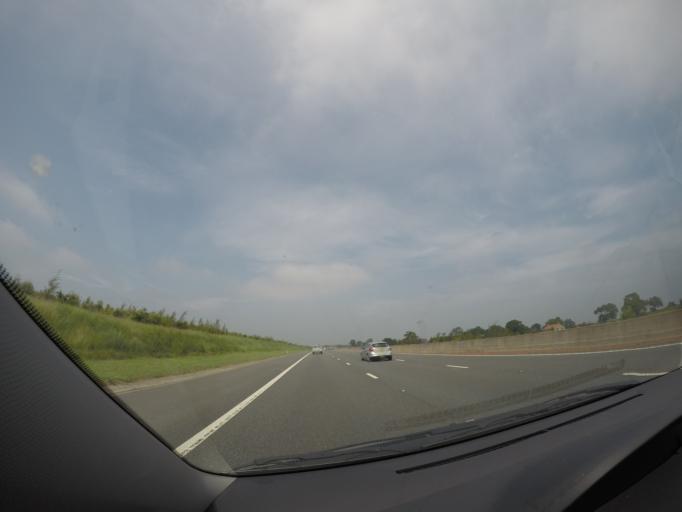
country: GB
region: England
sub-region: North Yorkshire
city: Bedale
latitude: 54.2610
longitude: -1.5165
